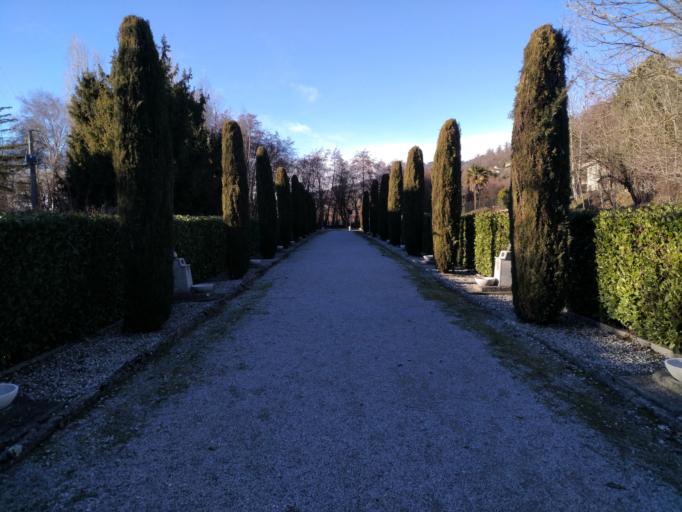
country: IT
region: Lombardy
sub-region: Provincia di Como
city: Montorfano
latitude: 45.7821
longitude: 9.1457
